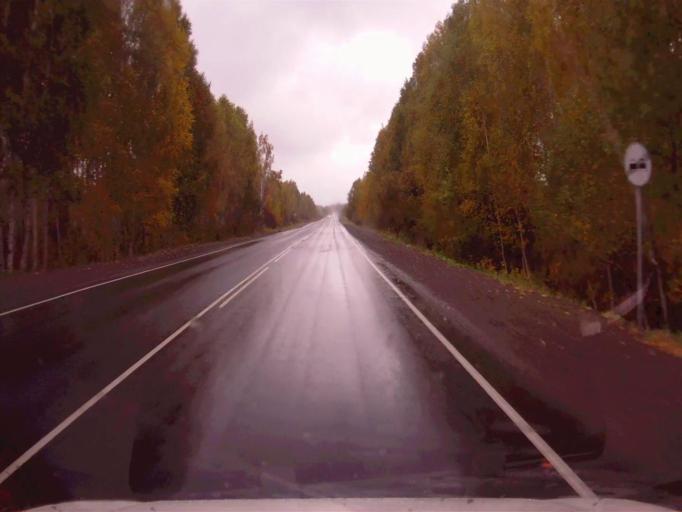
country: RU
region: Chelyabinsk
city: Argayash
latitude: 55.4793
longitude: 60.7594
